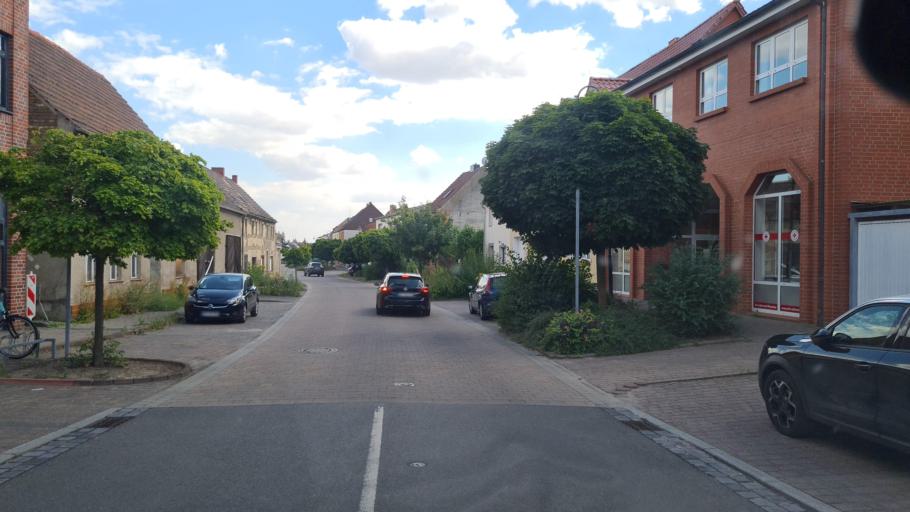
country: DE
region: Saxony-Anhalt
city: Zahna
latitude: 51.9120
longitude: 12.7869
